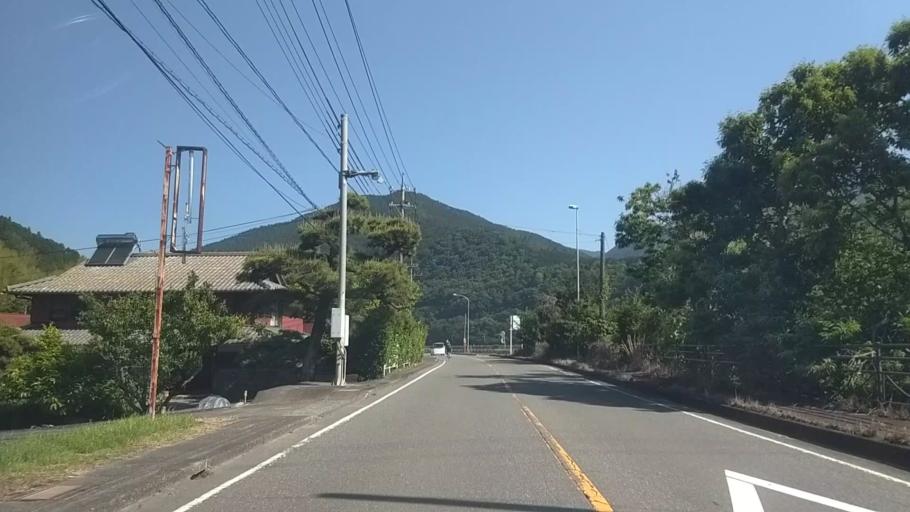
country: JP
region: Shizuoka
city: Fujinomiya
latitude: 35.2344
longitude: 138.5067
